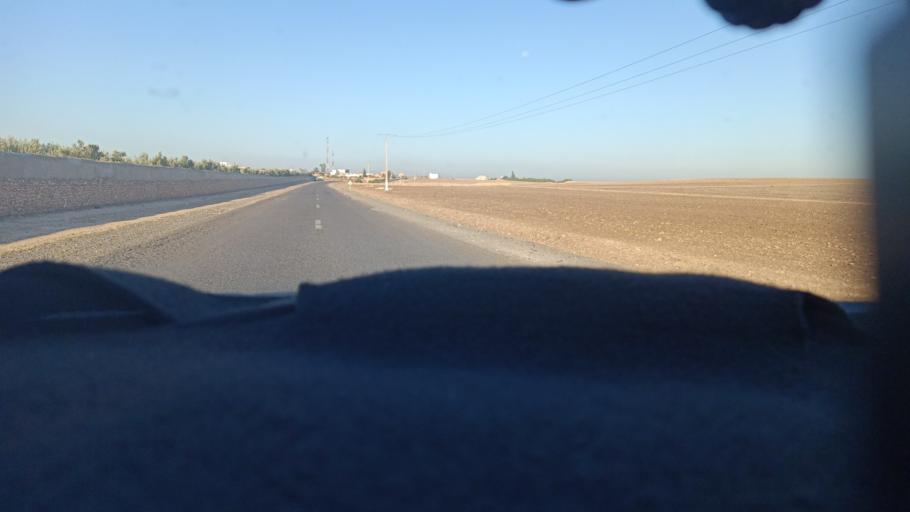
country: MA
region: Doukkala-Abda
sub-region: Safi
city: Youssoufia
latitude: 32.3707
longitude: -8.6690
